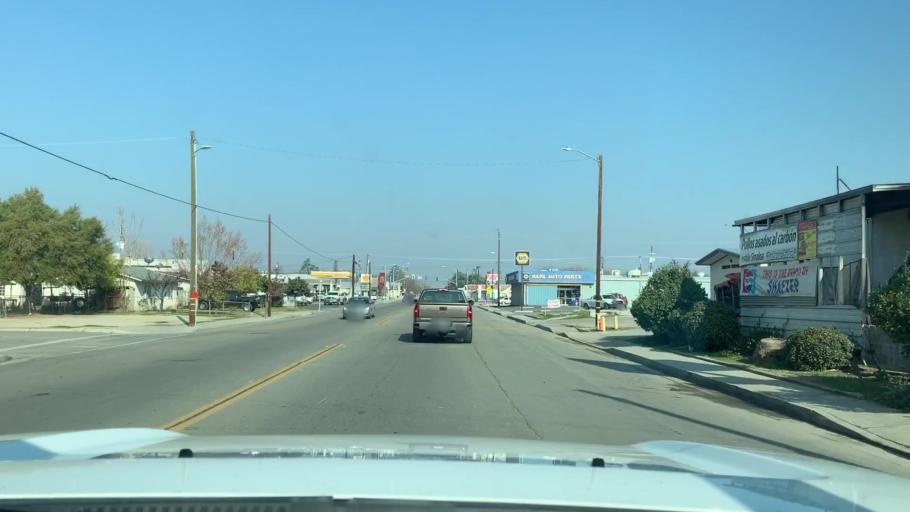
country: US
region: California
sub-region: Kern County
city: Shafter
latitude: 35.4978
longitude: -119.2783
